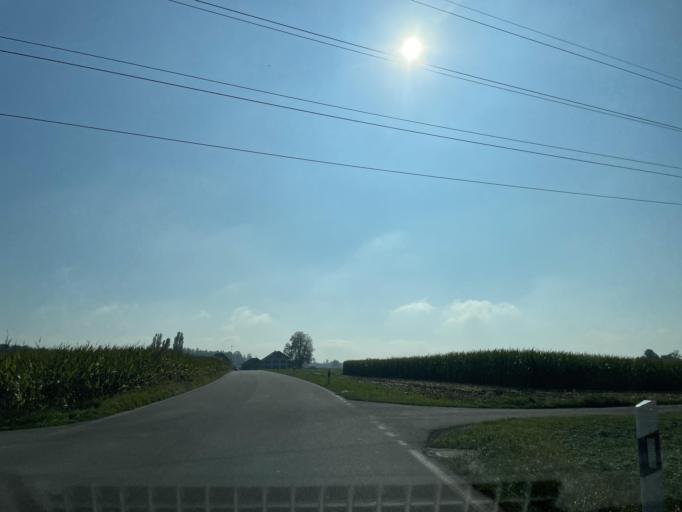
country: CH
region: Zurich
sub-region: Bezirk Winterthur
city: Brutten
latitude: 47.4667
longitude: 8.6674
